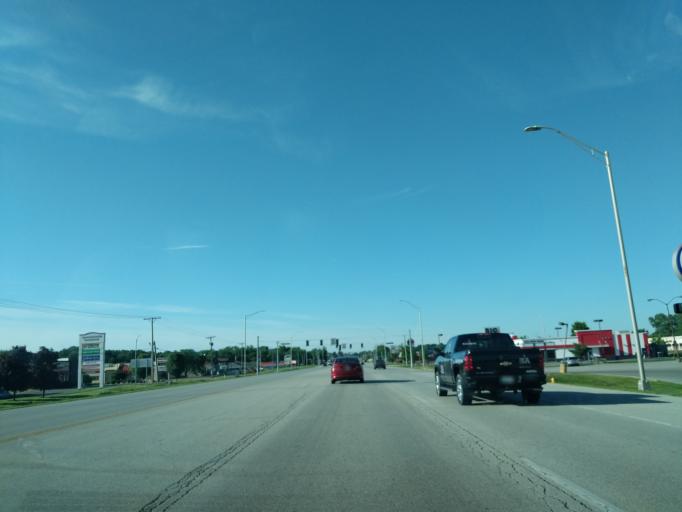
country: US
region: Indiana
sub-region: Hancock County
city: Greenfield
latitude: 39.8082
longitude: -85.7700
